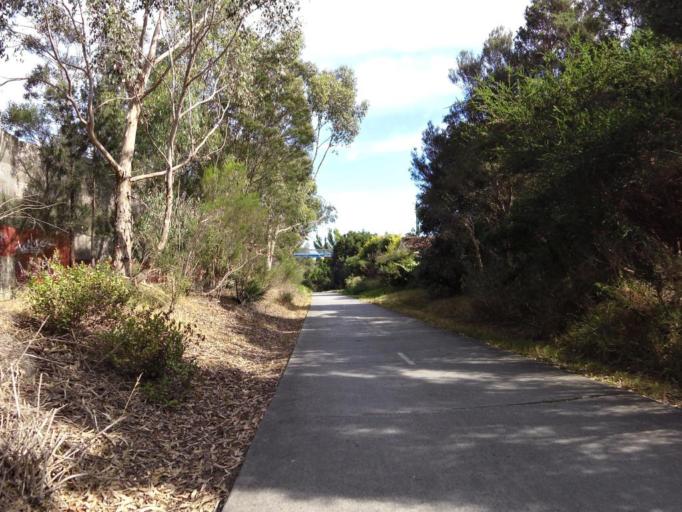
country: AU
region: Victoria
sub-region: Casey
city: Narre Warren
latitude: -38.0096
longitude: 145.3007
